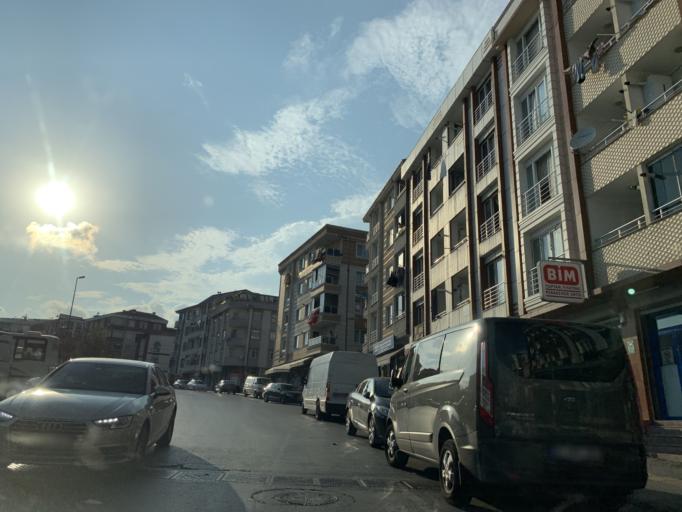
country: TR
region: Istanbul
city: Esenyurt
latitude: 41.0425
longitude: 28.6824
